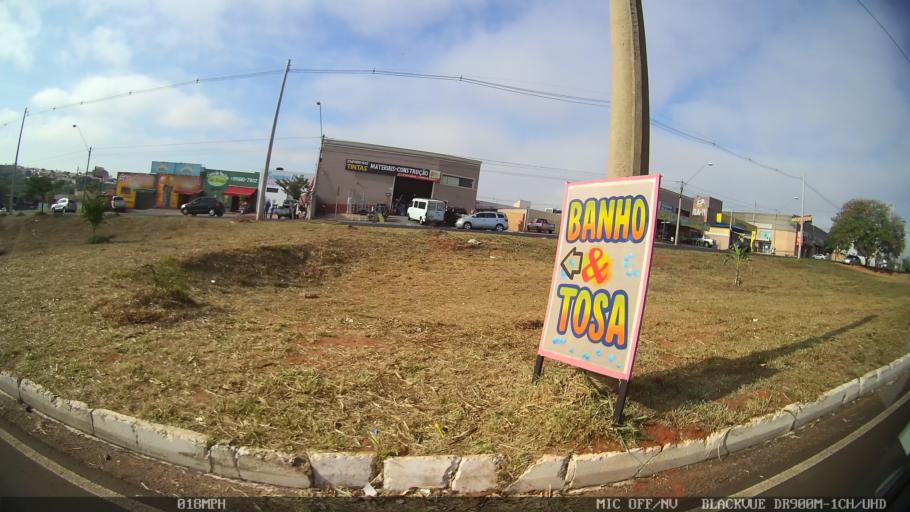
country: BR
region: Sao Paulo
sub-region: Sao Jose Do Rio Preto
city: Sao Jose do Rio Preto
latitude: -20.7971
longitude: -49.4283
